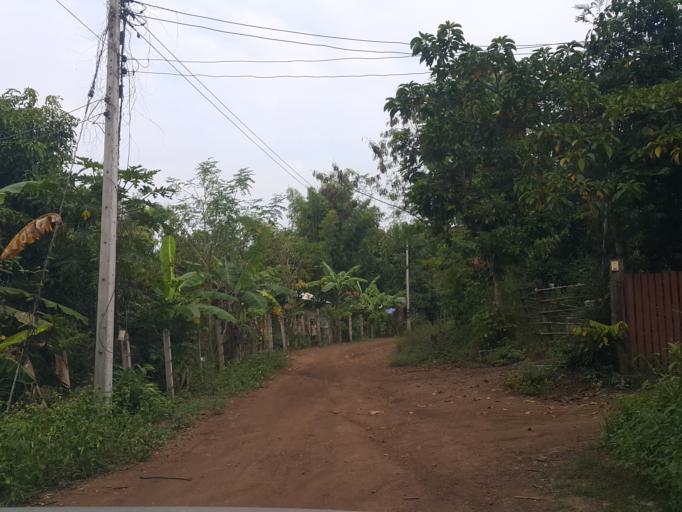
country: TH
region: Chiang Mai
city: Pai
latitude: 19.3627
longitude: 98.4509
